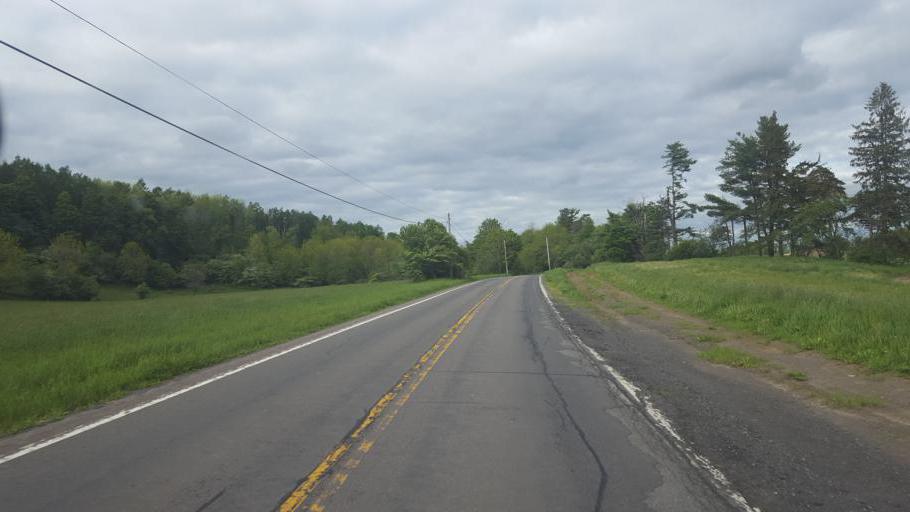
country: US
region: New York
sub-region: Otsego County
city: Richfield Springs
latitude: 42.8989
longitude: -74.9601
